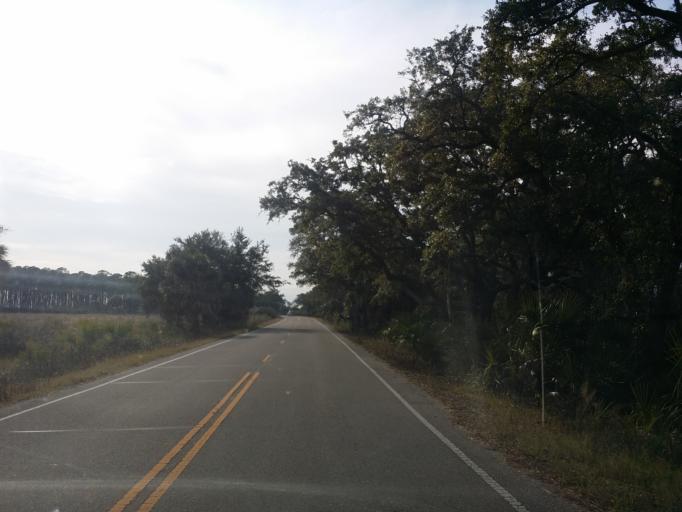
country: US
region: Florida
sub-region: Wakulla County
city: Crawfordville
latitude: 30.0863
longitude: -84.1669
